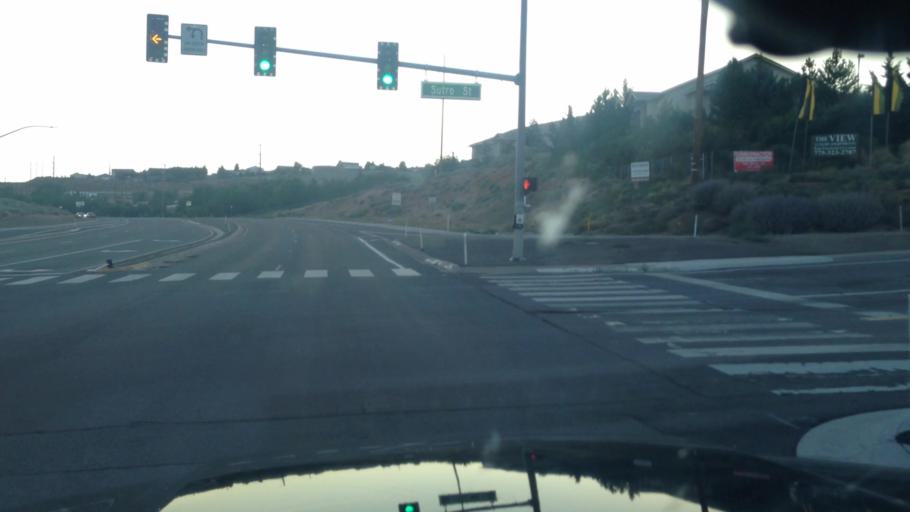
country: US
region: Nevada
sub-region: Washoe County
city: Reno
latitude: 39.5566
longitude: -119.7984
